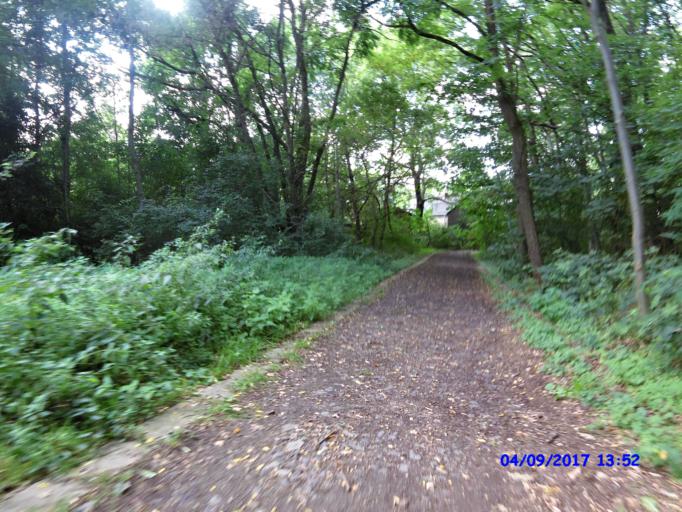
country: DE
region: Saxony
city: Taucha
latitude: 51.3540
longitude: 12.4679
